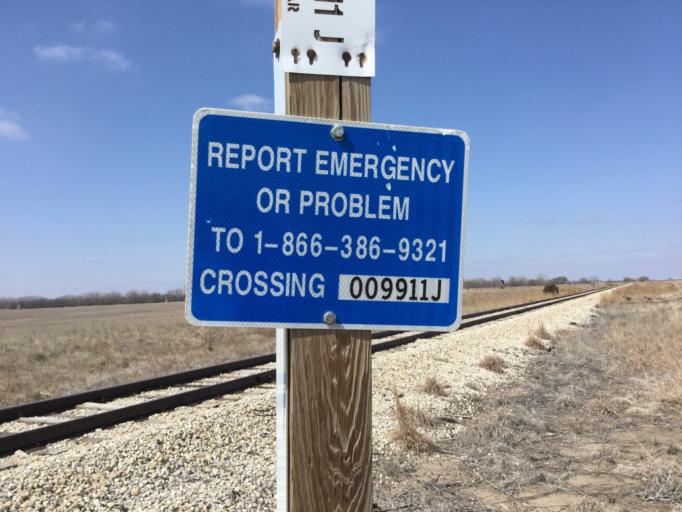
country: US
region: Kansas
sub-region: Barton County
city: Ellinwood
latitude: 38.3310
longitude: -98.5168
